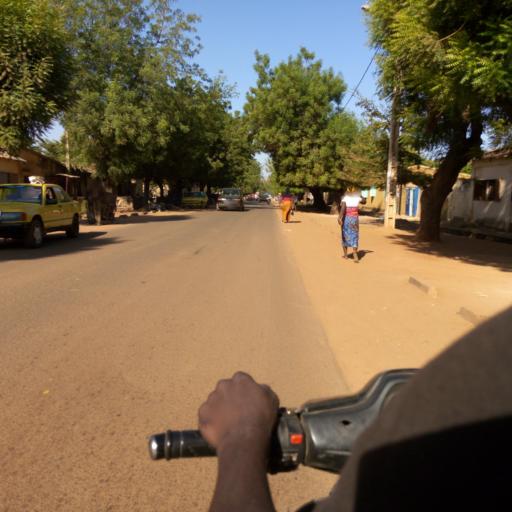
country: ML
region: Bamako
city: Bamako
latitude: 12.6556
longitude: -8.0171
